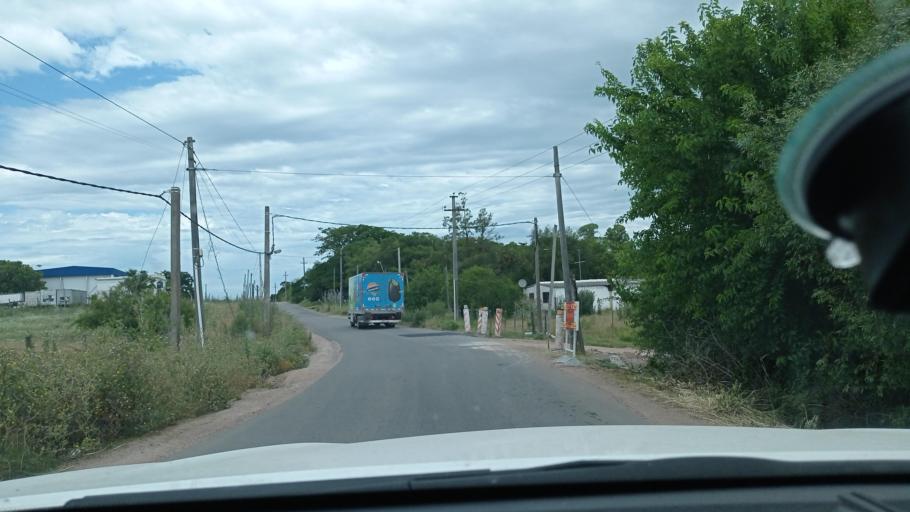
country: UY
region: Canelones
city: La Paz
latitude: -34.8021
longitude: -56.1904
